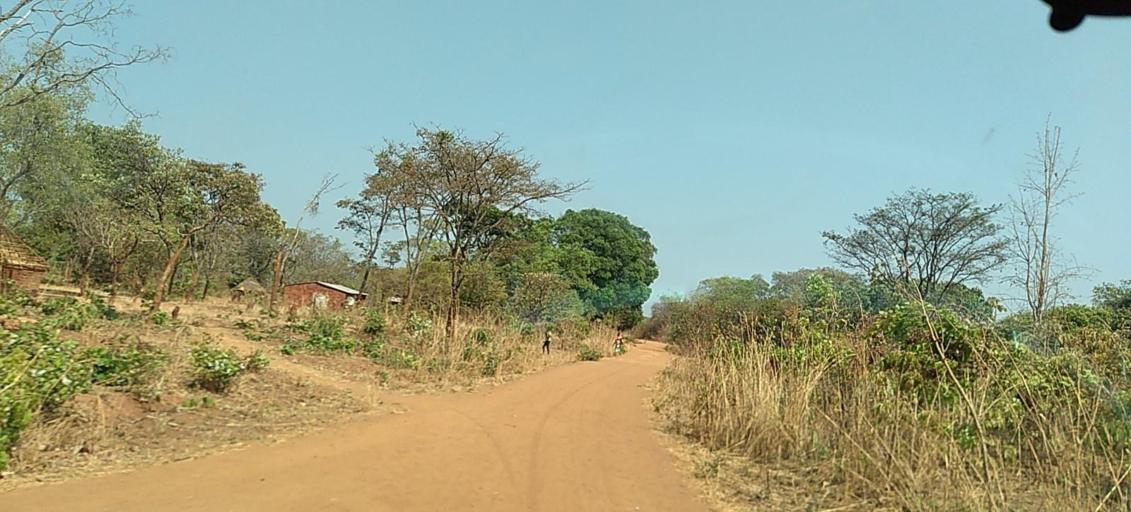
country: ZM
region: North-Western
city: Kasempa
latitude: -13.3900
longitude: 25.6801
